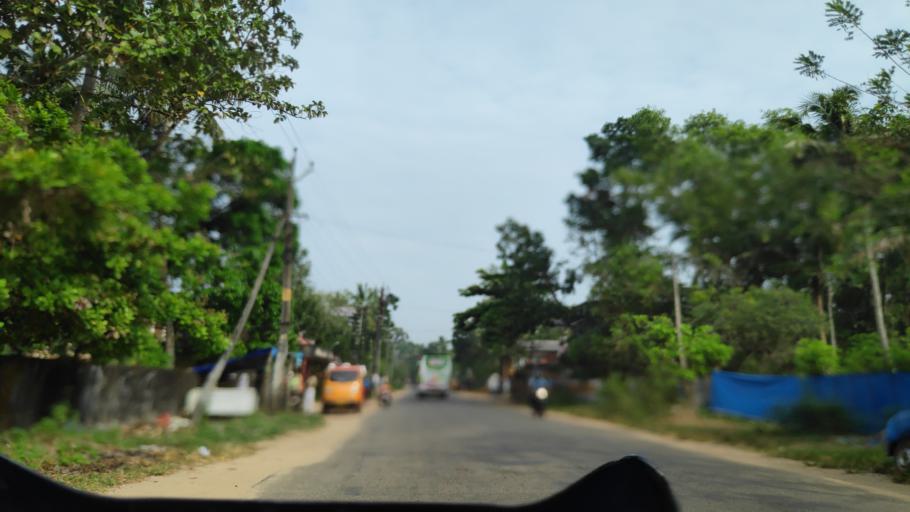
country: IN
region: Kerala
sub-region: Alappuzha
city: Kutiatodu
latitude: 9.8093
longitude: 76.3528
